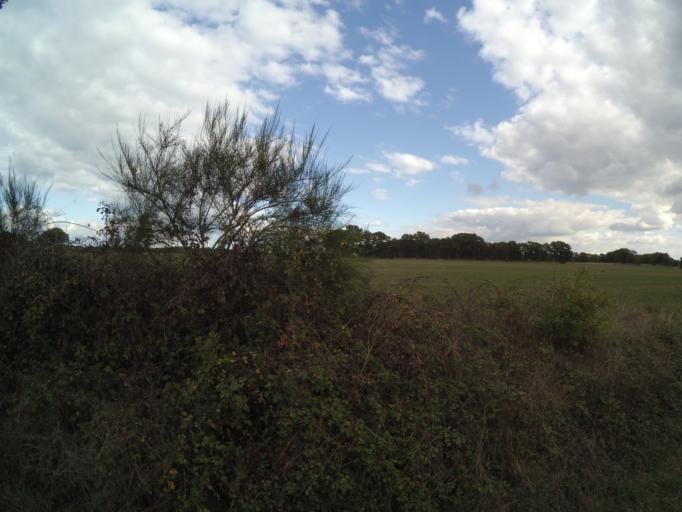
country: FR
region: Pays de la Loire
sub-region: Departement de la Loire-Atlantique
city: Remouille
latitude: 47.0681
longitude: -1.3686
